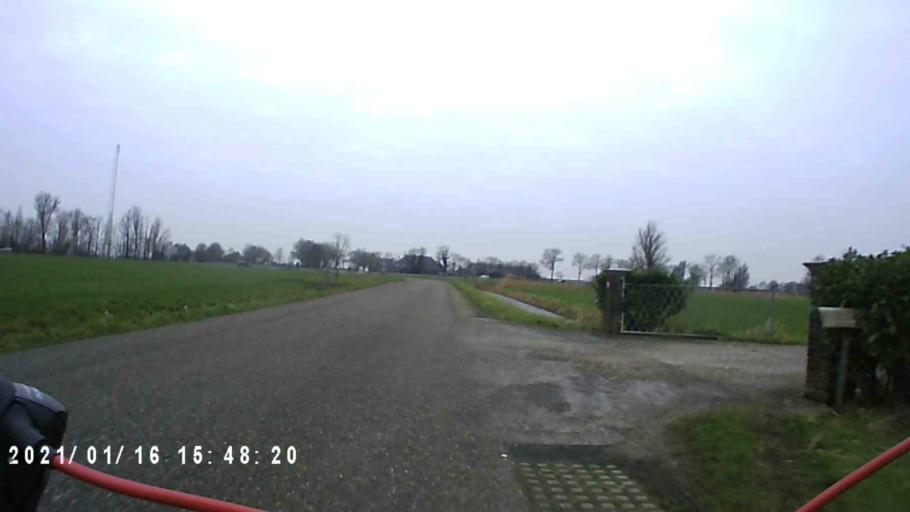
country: NL
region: Groningen
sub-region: Gemeente Winsum
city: Winsum
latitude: 53.2832
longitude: 6.5379
